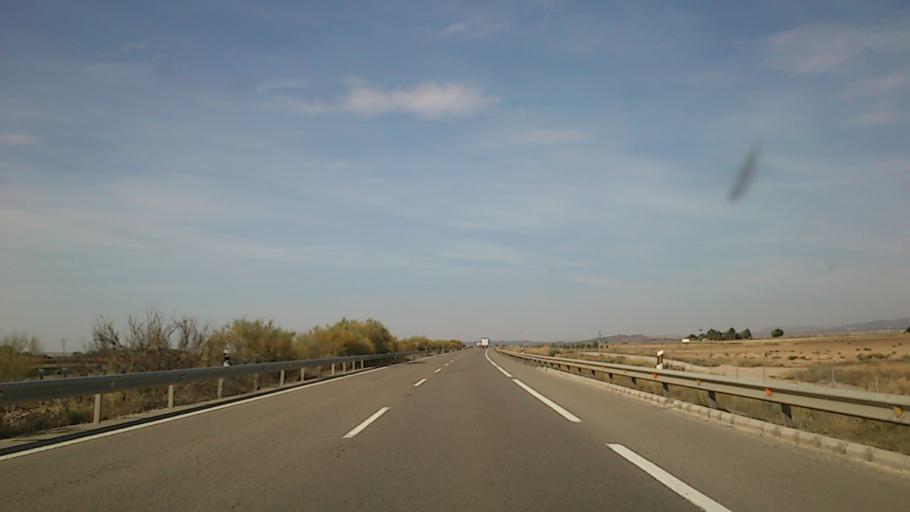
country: ES
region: Aragon
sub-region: Provincia de Teruel
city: Fuentes Claras
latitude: 40.8585
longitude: -1.3091
